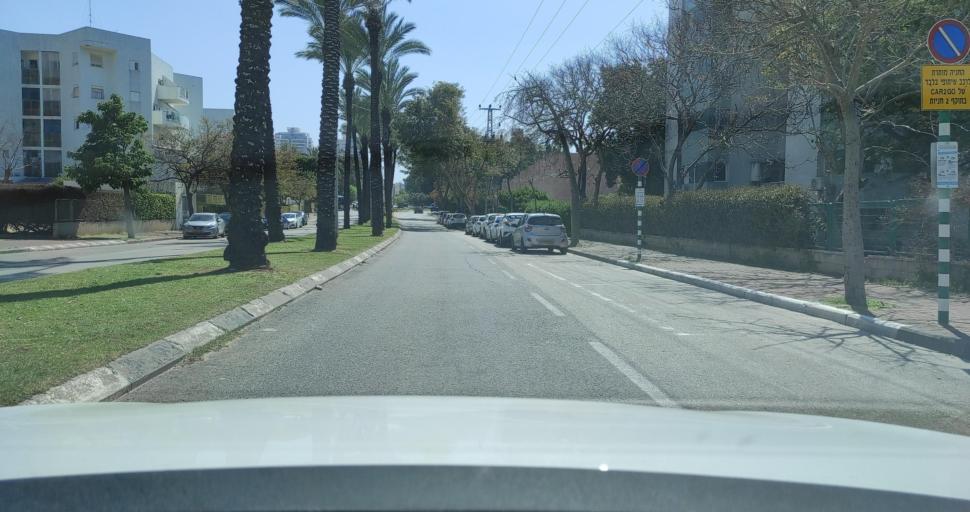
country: IL
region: Central District
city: Nordiyya
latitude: 32.3085
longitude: 34.8810
